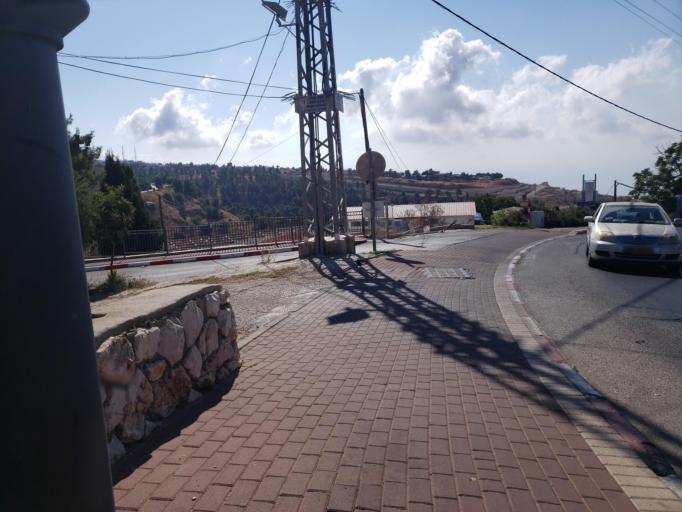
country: IL
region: Northern District
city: Safed
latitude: 32.9635
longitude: 35.4987
